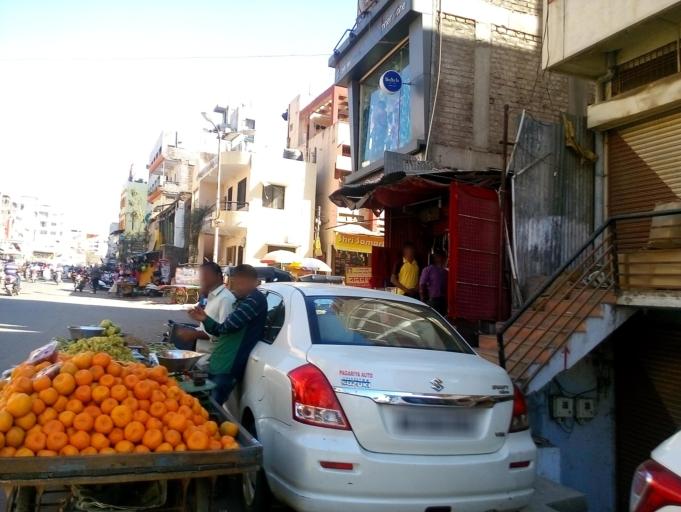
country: IN
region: Maharashtra
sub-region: Aurangabad Division
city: Aurangabad
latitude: 19.8847
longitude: 75.3283
